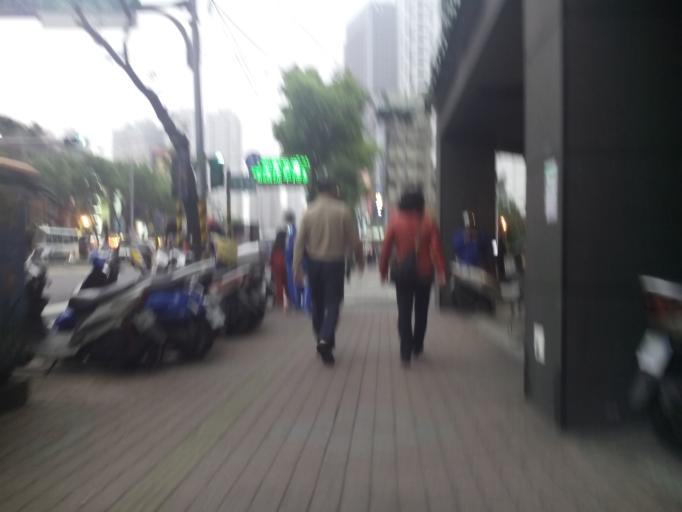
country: TW
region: Taipei
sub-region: Taipei
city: Banqiao
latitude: 25.0205
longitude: 121.4664
